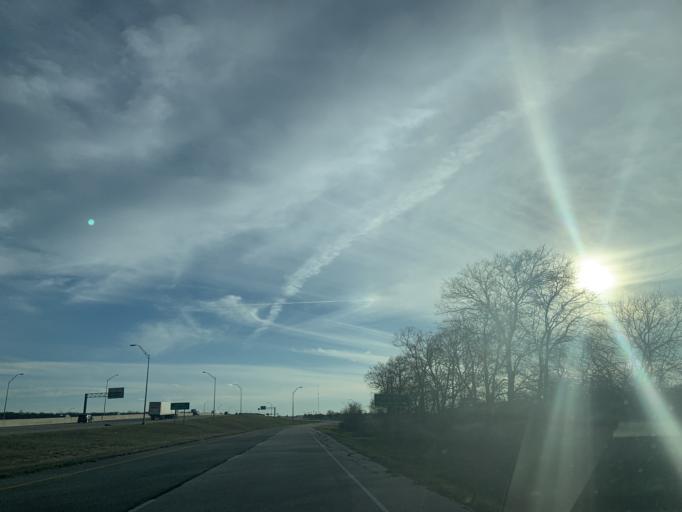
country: US
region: Texas
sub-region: Bell County
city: Salado
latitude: 30.8777
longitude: -97.5803
